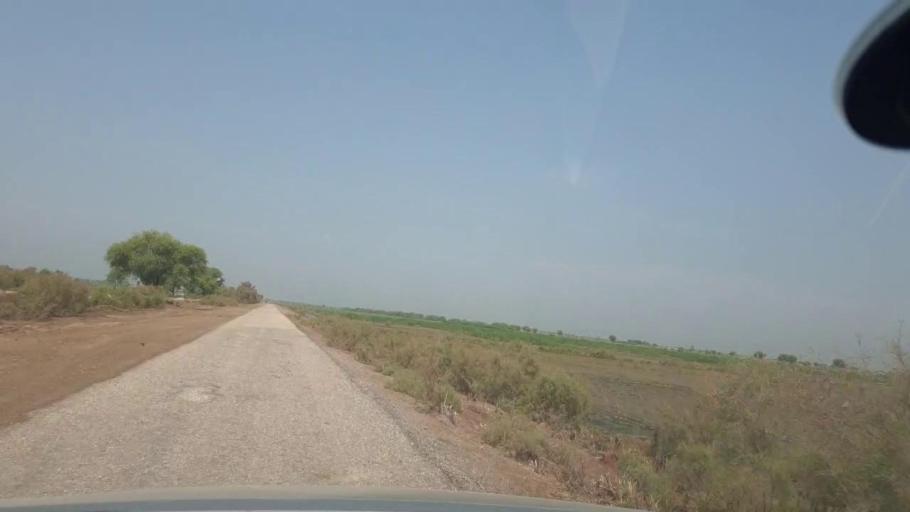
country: PK
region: Balochistan
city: Mehrabpur
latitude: 28.0619
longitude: 68.0677
